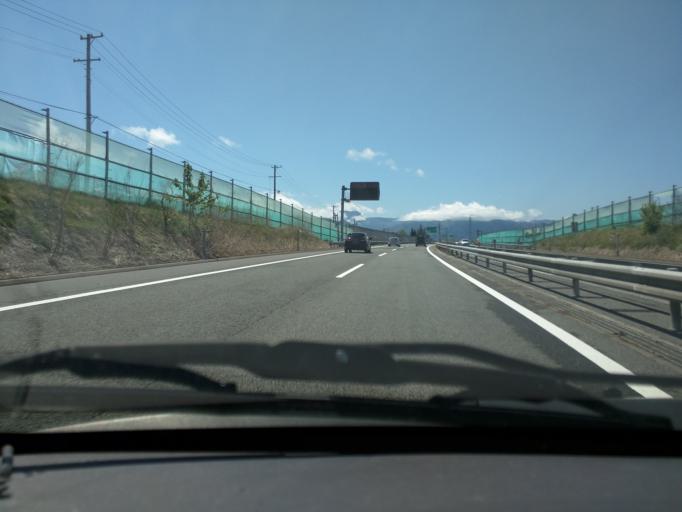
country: JP
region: Nagano
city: Nakano
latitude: 36.7355
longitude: 138.3180
